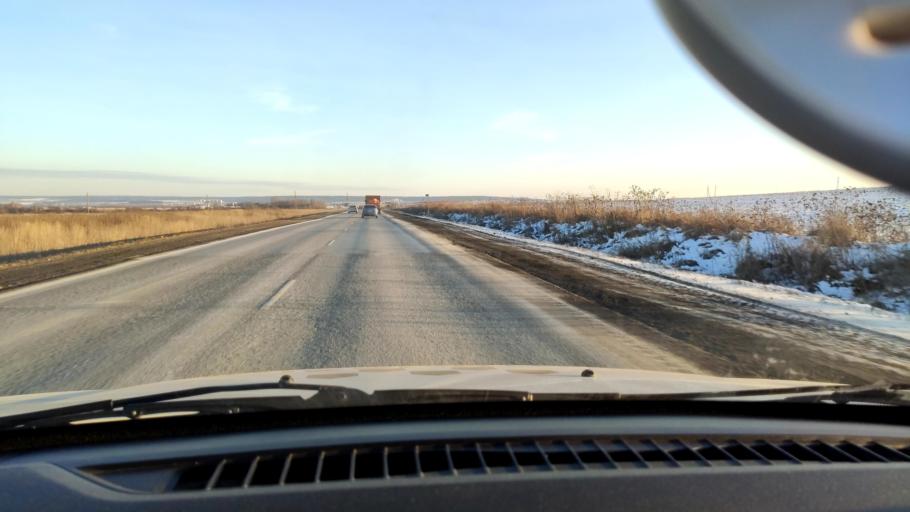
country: RU
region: Perm
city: Froly
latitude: 57.9014
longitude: 56.2147
